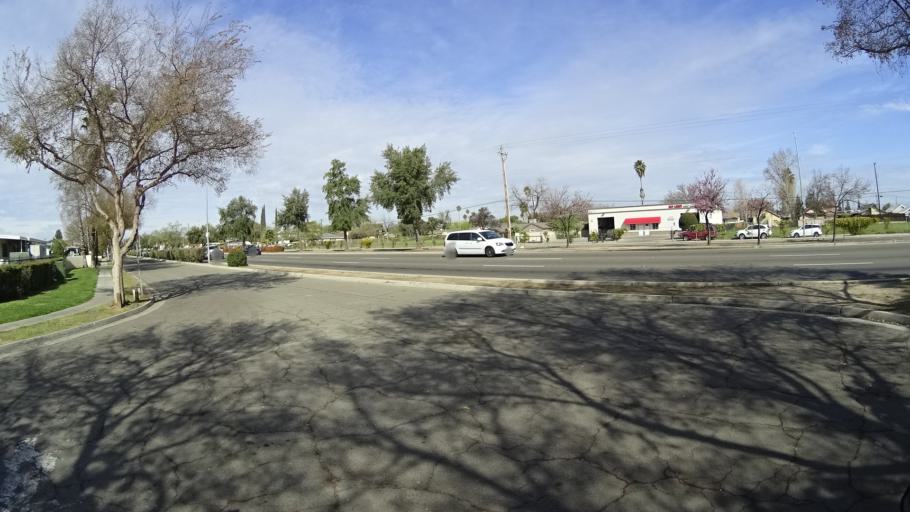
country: US
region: California
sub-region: Fresno County
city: Clovis
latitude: 36.8370
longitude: -119.7921
